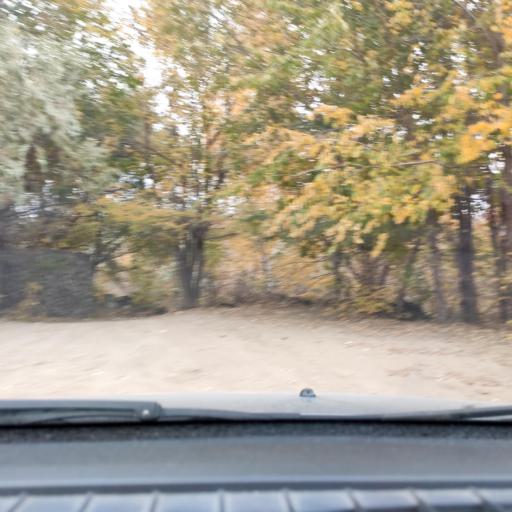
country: RU
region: Samara
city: Tol'yatti
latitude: 53.4991
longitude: 49.2599
